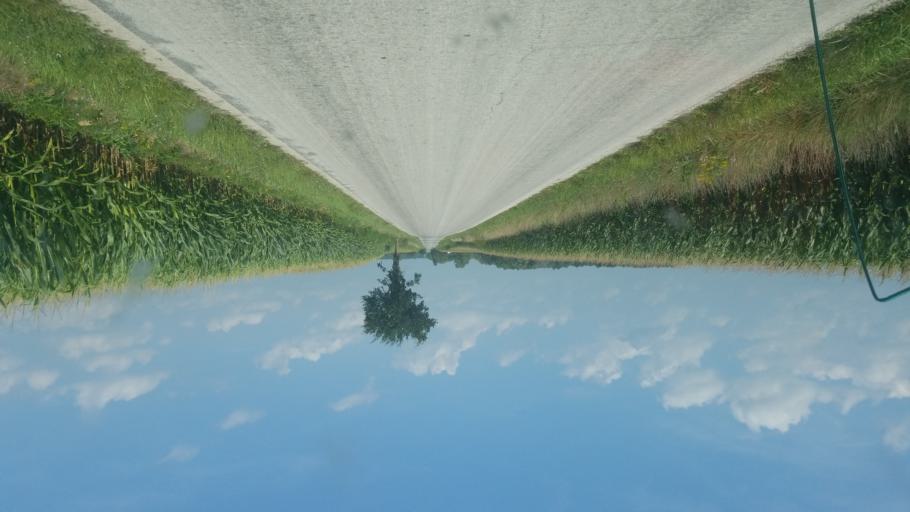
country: US
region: Ohio
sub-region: Huron County
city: Greenwich
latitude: 40.9547
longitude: -82.4315
